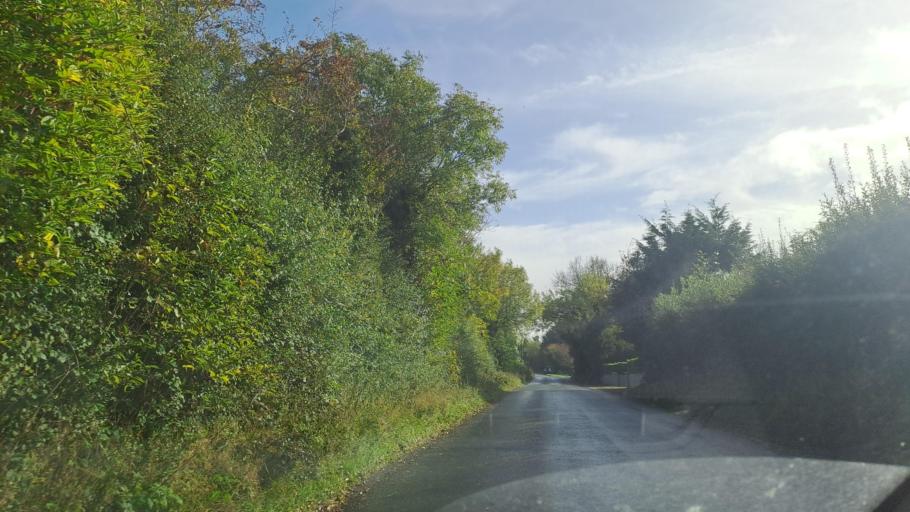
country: IE
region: Ulster
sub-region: County Monaghan
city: Carrickmacross
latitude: 53.8734
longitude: -6.6677
